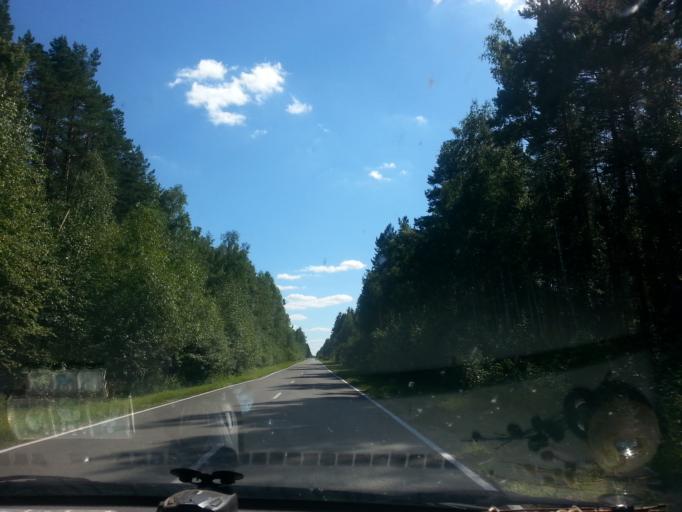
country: RU
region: Vladimir
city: Galitsy
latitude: 56.0825
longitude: 42.8681
